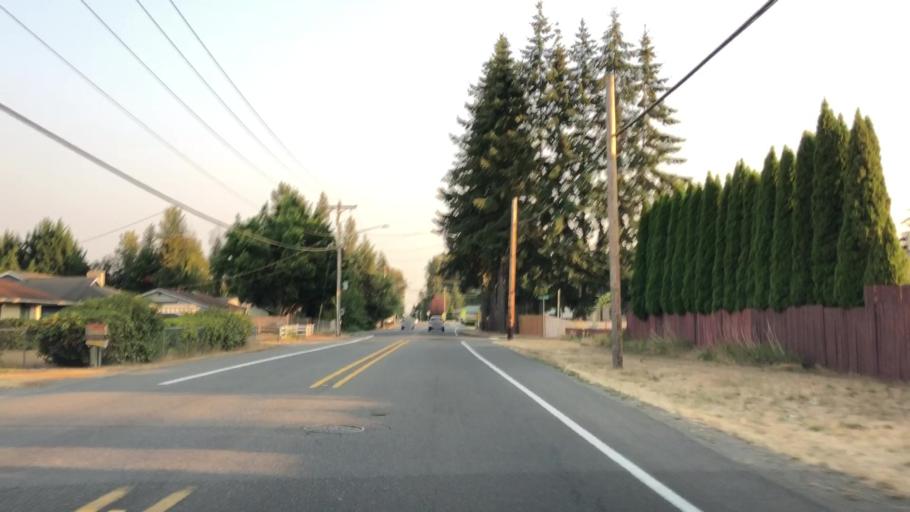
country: US
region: Washington
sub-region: Snohomish County
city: Marysville
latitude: 48.0949
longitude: -122.1622
